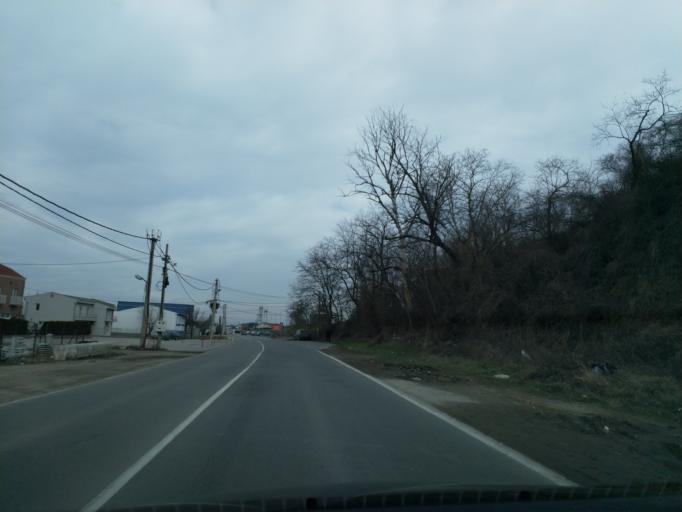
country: RS
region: Central Serbia
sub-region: Belgrade
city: Zvezdara
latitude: 44.7297
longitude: 20.5833
